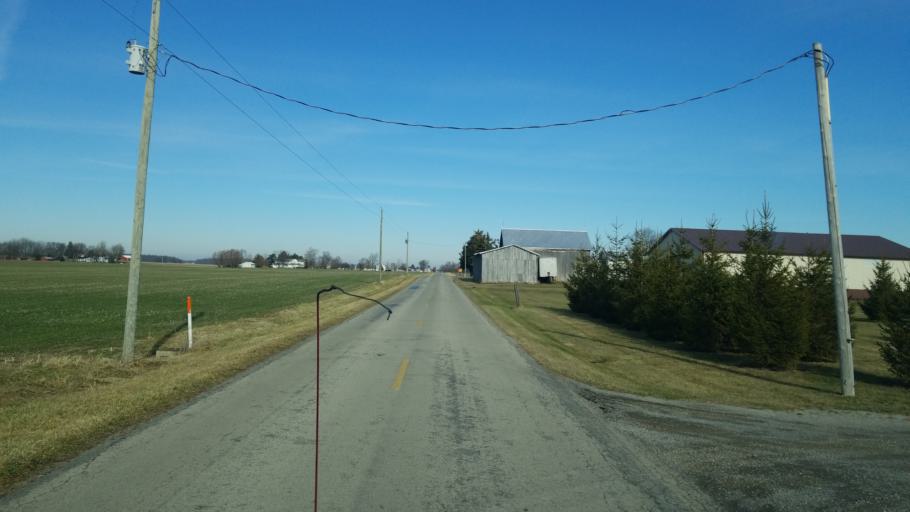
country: US
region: Ohio
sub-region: Putnam County
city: Pandora
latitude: 40.9124
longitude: -83.9377
